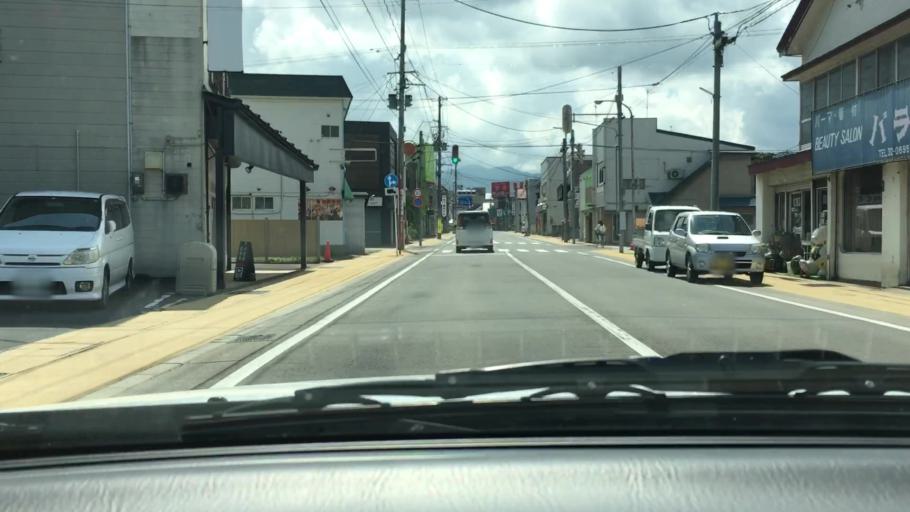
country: JP
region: Aomori
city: Hirosaki
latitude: 40.5936
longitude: 140.4735
